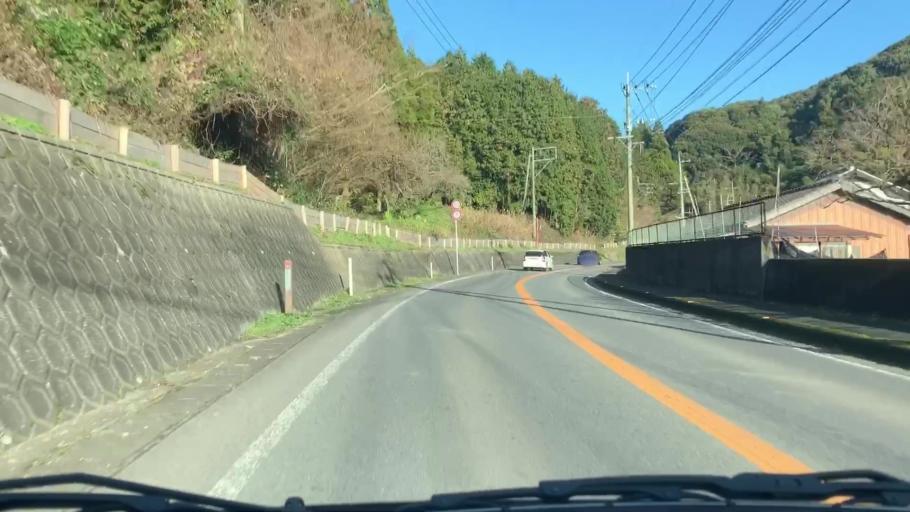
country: JP
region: Saga Prefecture
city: Takeocho-takeo
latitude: 33.2359
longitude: 130.0123
